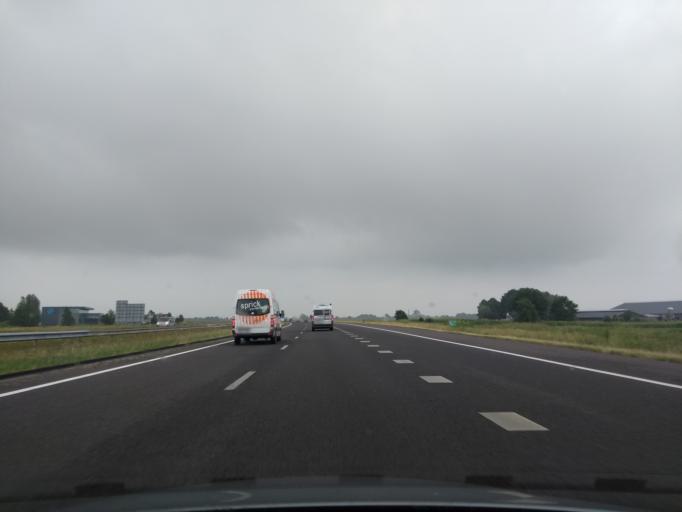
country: NL
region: Friesland
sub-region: Gemeente Skarsterlan
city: Joure
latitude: 52.9618
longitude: 5.7703
